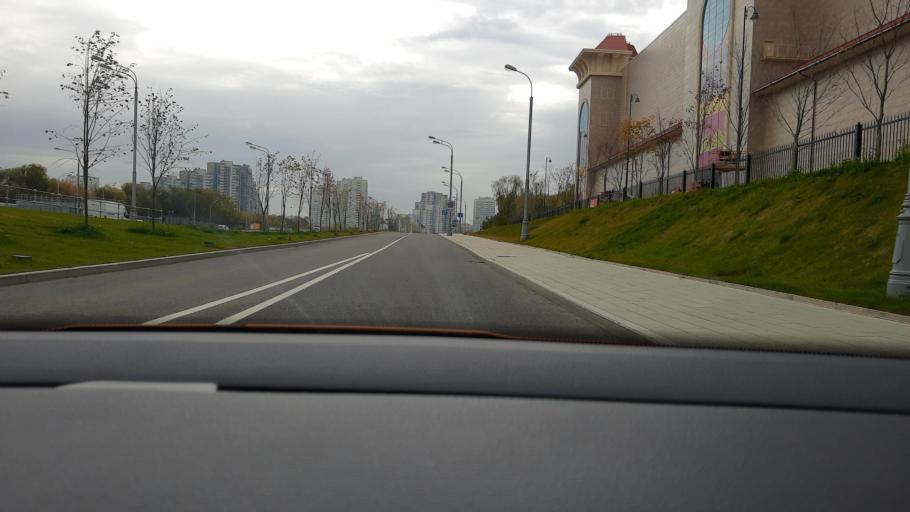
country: RU
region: Moskovskaya
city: Kozhukhovo
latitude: 55.6946
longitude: 37.6809
